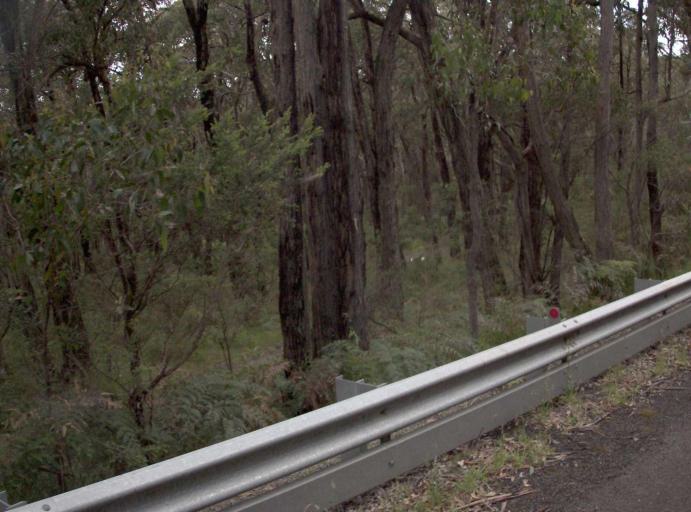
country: AU
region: Victoria
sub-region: Mornington Peninsula
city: Dromana
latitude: -38.3582
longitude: 144.9678
